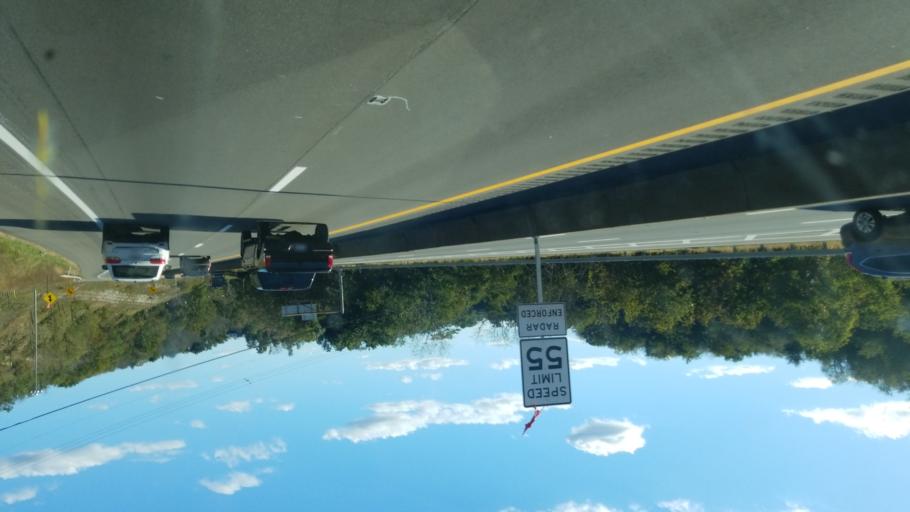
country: US
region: West Virginia
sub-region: Ohio County
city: Bethlehem
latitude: 40.0506
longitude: -80.6970
